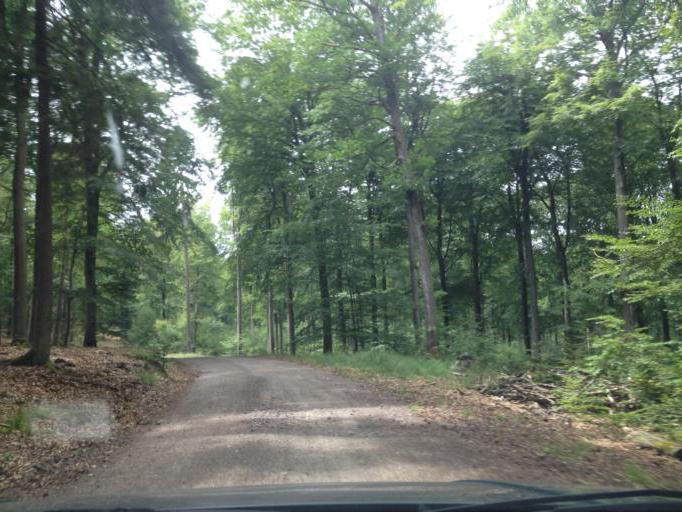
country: DE
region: Rheinland-Pfalz
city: Elmstein
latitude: 49.3006
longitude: 7.8854
